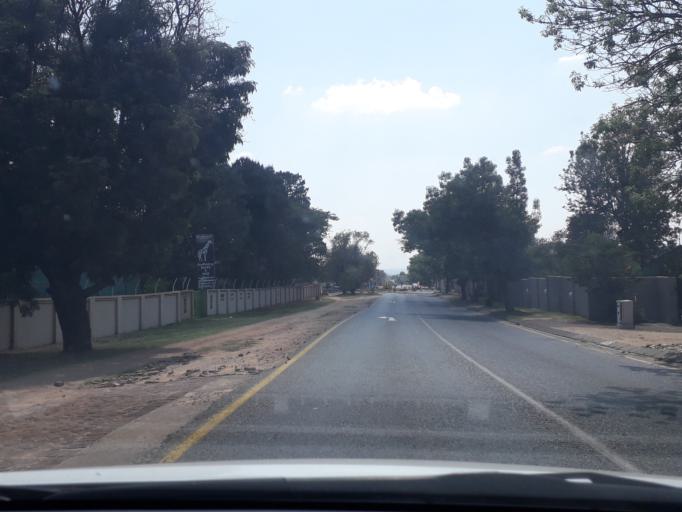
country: ZA
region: Gauteng
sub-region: West Rand District Municipality
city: Muldersdriseloop
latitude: -26.0756
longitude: 27.9304
